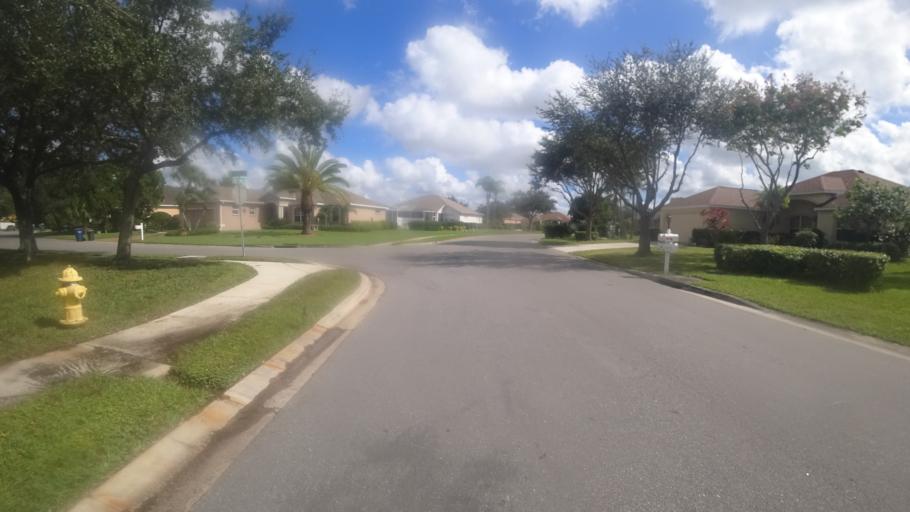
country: US
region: Florida
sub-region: Manatee County
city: Ellenton
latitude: 27.4937
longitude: -82.4375
